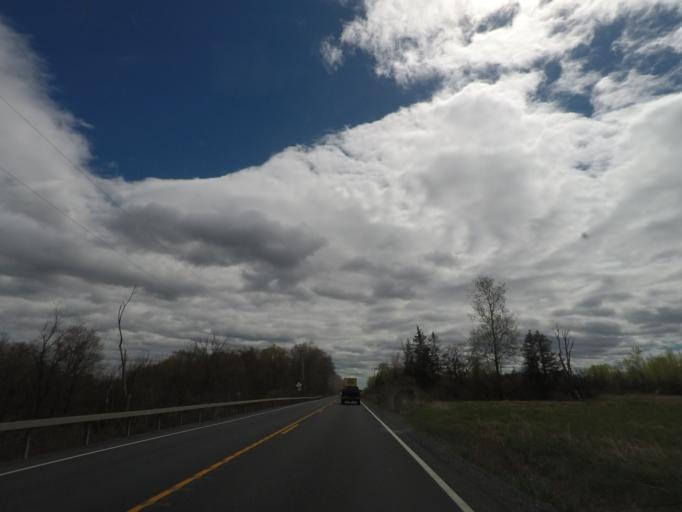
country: US
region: New York
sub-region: Albany County
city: Ravena
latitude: 42.4970
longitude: -73.7950
